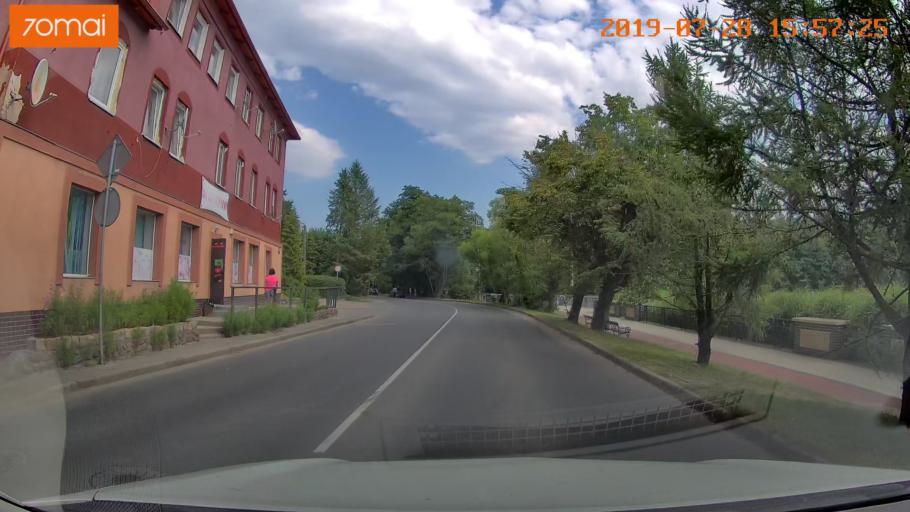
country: RU
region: Kaliningrad
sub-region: Gorod Svetlogorsk
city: Svetlogorsk
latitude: 54.9381
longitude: 20.1550
